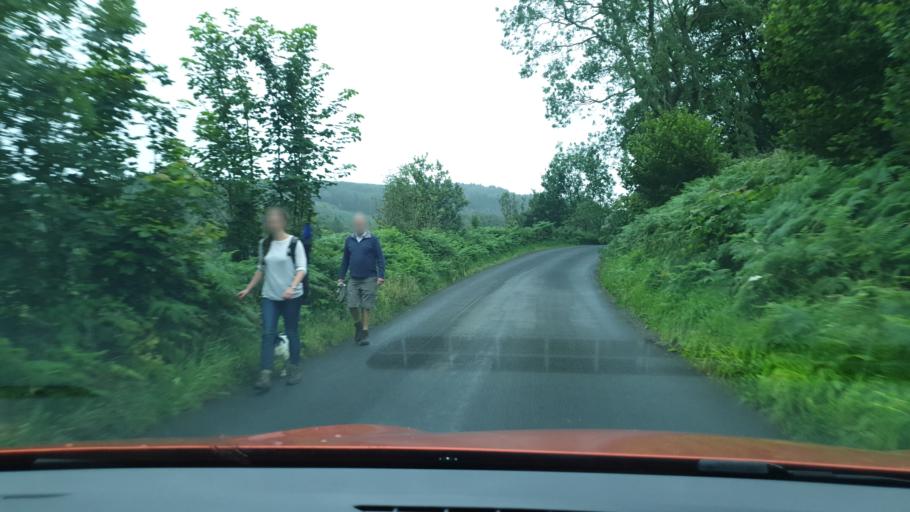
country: GB
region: England
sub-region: Cumbria
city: Seascale
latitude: 54.4146
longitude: -3.3579
